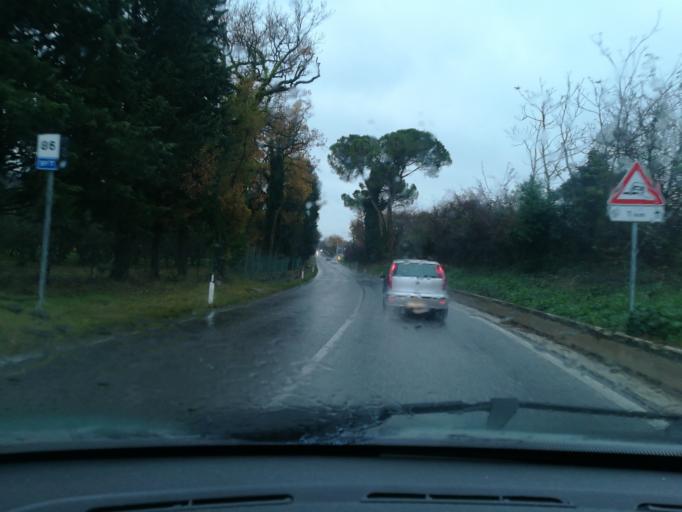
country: IT
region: The Marches
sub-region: Provincia di Macerata
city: Sforzacosta
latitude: 43.2727
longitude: 13.4272
